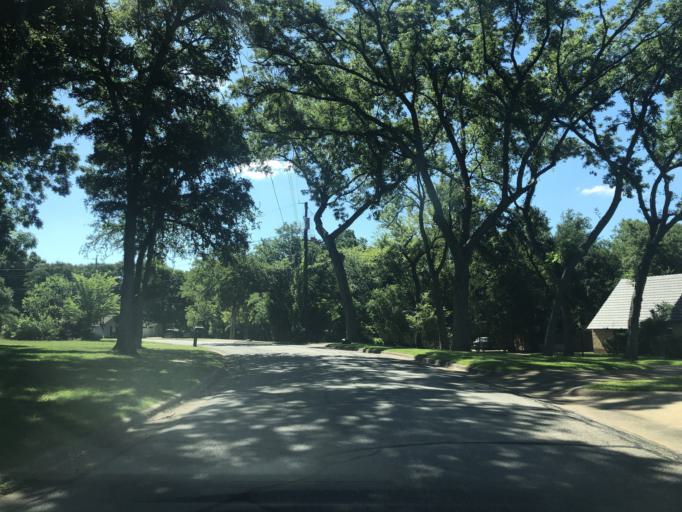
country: US
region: Texas
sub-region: Dallas County
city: Duncanville
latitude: 32.6383
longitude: -96.9362
